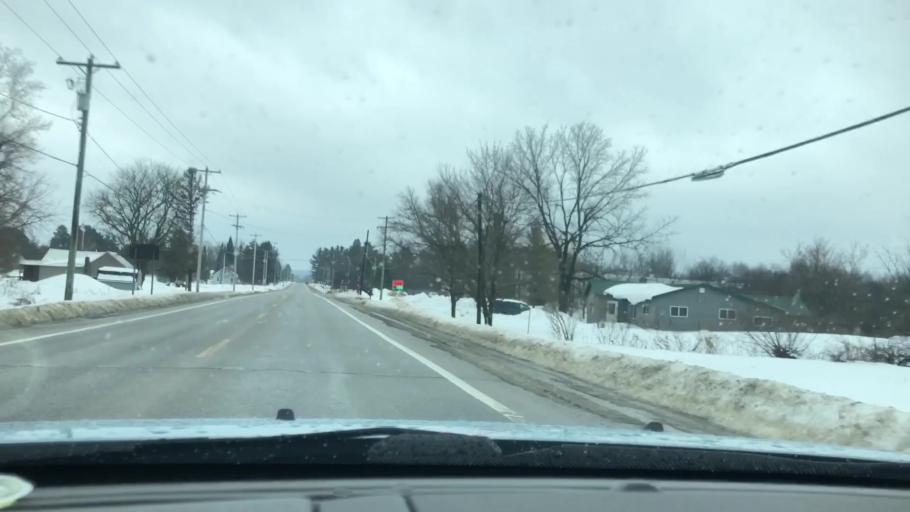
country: US
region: Michigan
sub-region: Charlevoix County
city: East Jordan
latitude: 45.1499
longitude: -85.1192
